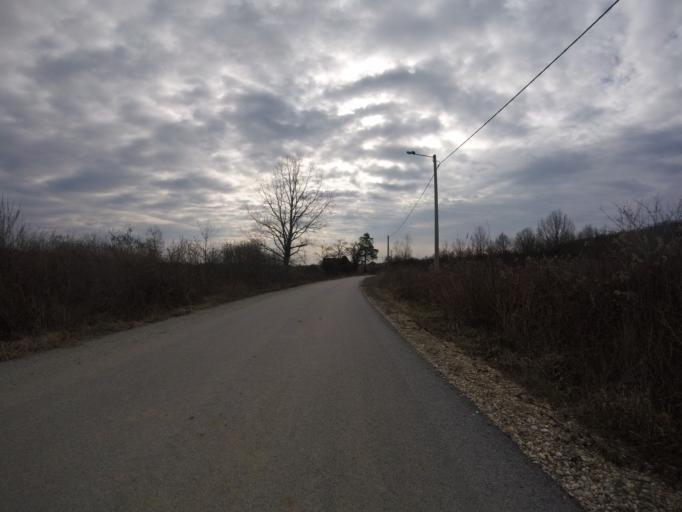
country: HR
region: Sisacko-Moslavacka
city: Glina
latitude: 45.4494
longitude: 16.0672
